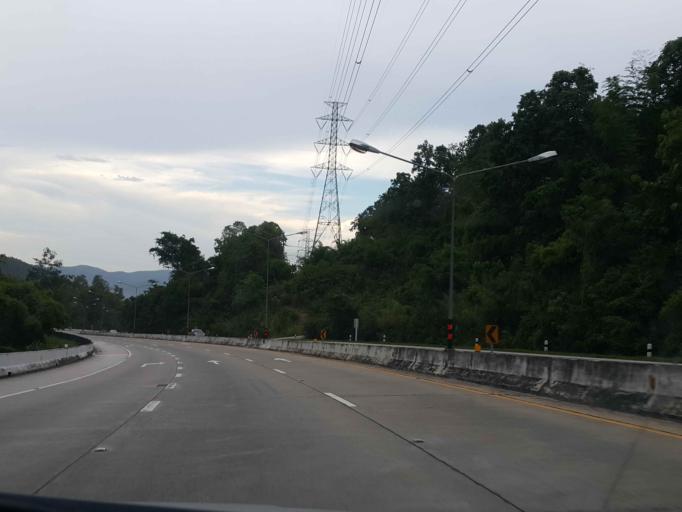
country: TH
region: Lamphun
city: Mae Tha
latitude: 18.4271
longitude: 99.2082
